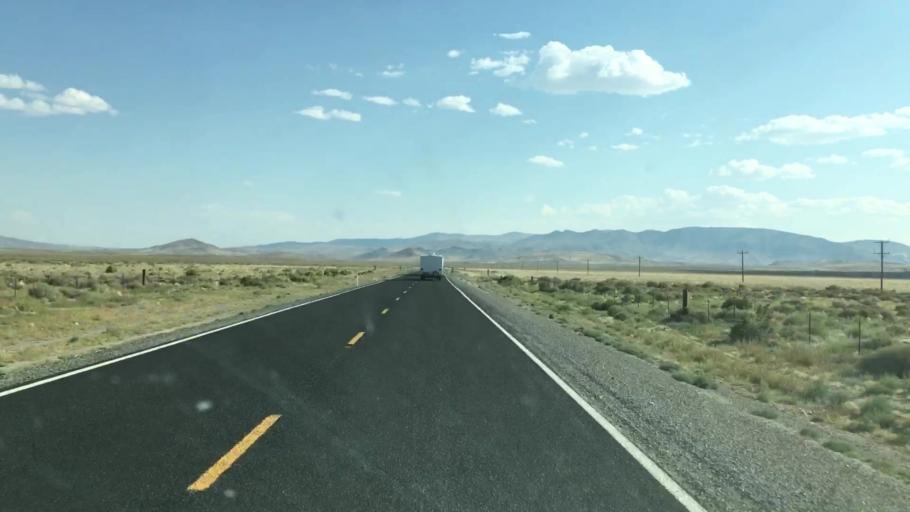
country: US
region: Nevada
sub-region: Lyon County
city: Fernley
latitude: 39.6848
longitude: -119.3350
